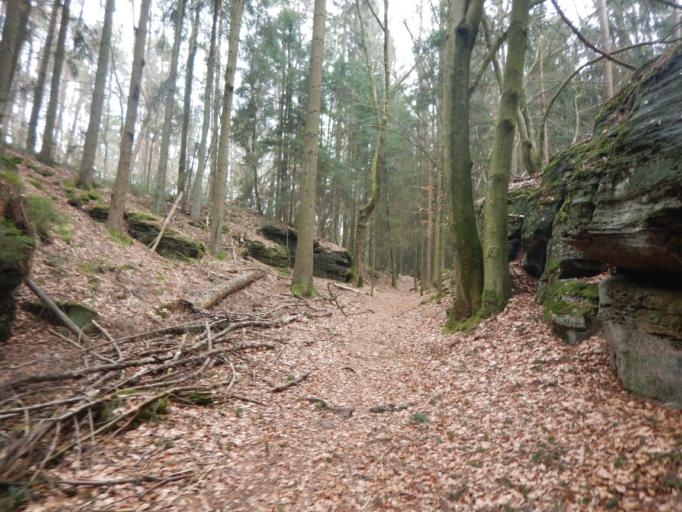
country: LU
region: Grevenmacher
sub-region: Canton d'Echternach
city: Beaufort
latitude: 49.8453
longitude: 6.3060
